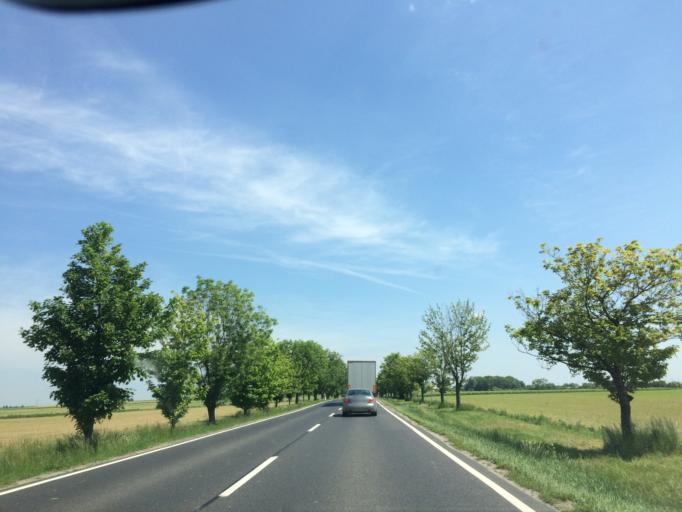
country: PL
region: Lower Silesian Voivodeship
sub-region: Powiat wroclawski
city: Gniechowice
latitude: 51.0019
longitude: 16.8529
